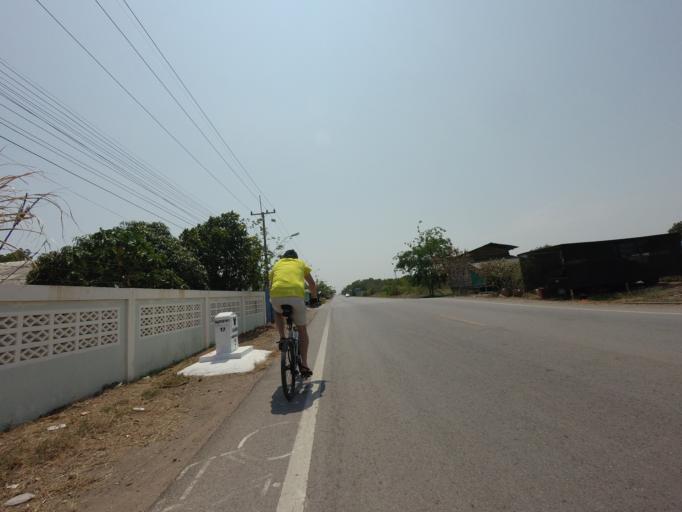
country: TH
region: Samut Sakhon
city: Samut Sakhon
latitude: 13.5144
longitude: 100.3917
